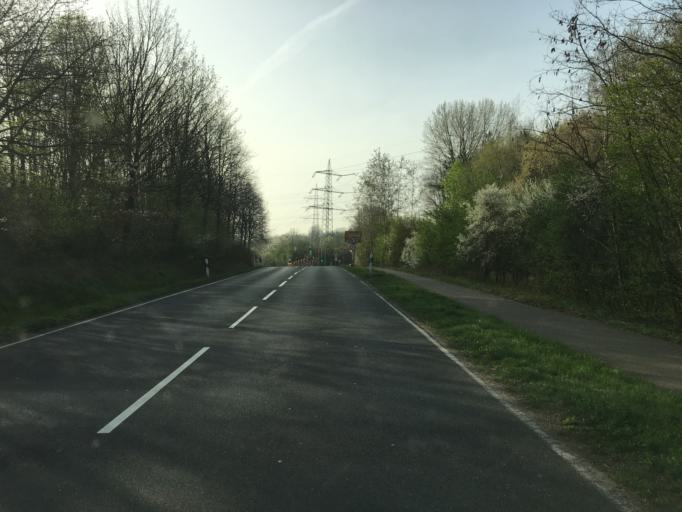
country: DE
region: North Rhine-Westphalia
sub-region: Regierungsbezirk Koln
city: Hurth
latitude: 50.8654
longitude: 6.8544
